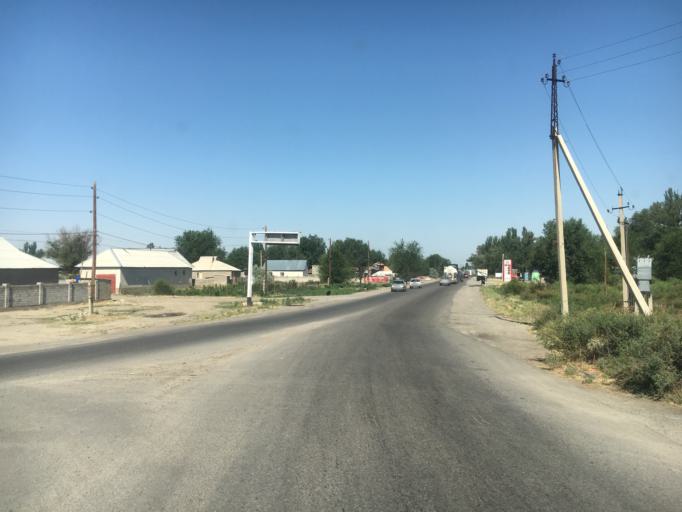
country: KZ
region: Zhambyl
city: Taraz
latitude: 42.9426
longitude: 71.4142
